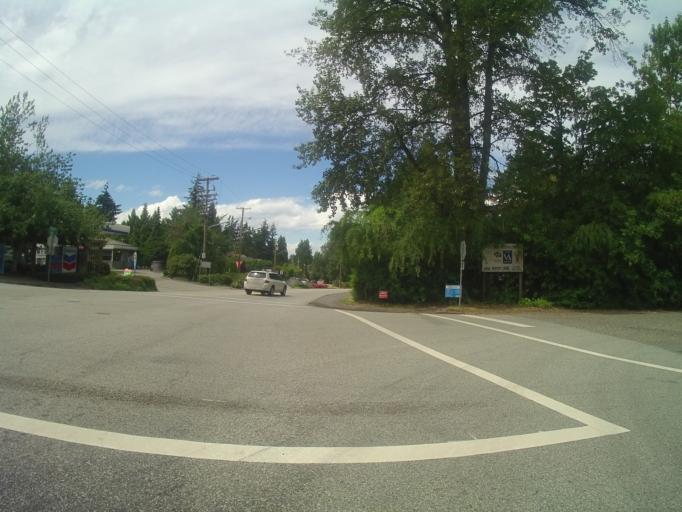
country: CA
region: British Columbia
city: Surrey
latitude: 49.0531
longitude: -122.8672
